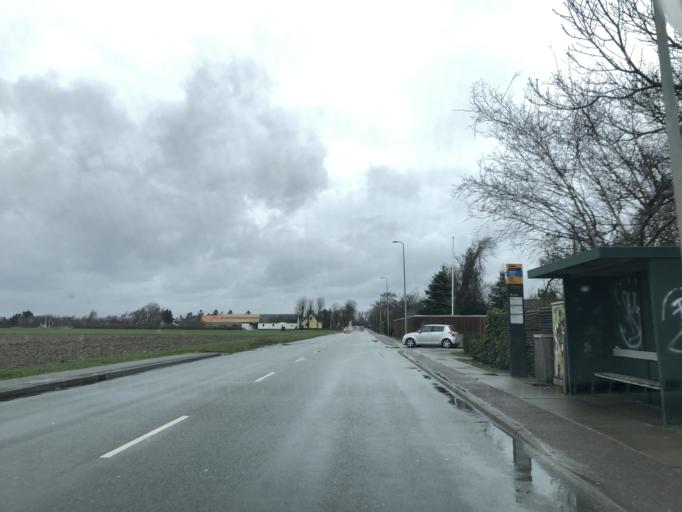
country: DK
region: Capital Region
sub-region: Dragor Kommune
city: Dragor
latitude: 55.5883
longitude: 12.6354
